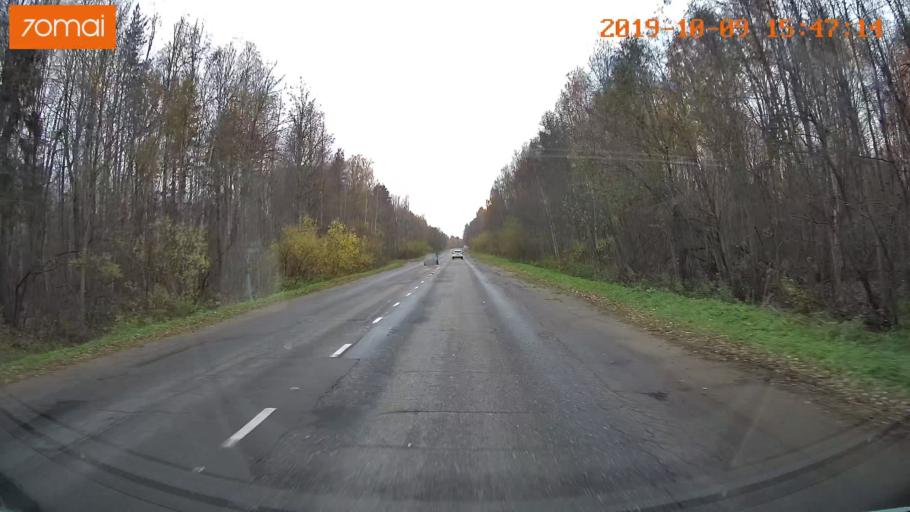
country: RU
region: Kostroma
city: Oktyabr'skiy
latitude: 57.8188
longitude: 41.0315
